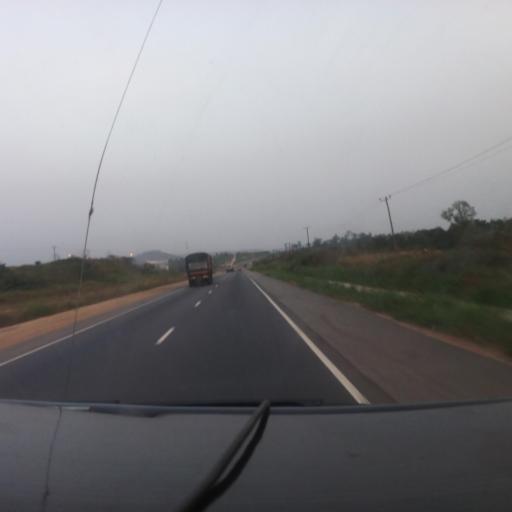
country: GH
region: Eastern
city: Nsawam
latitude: 5.8688
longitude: -0.3663
